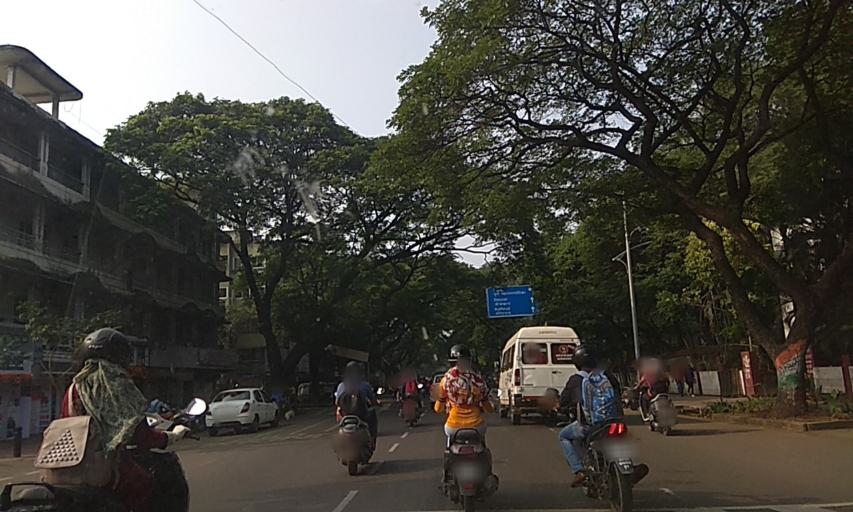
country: IN
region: Maharashtra
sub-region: Pune Division
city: Shivaji Nagar
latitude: 18.5267
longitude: 73.8507
